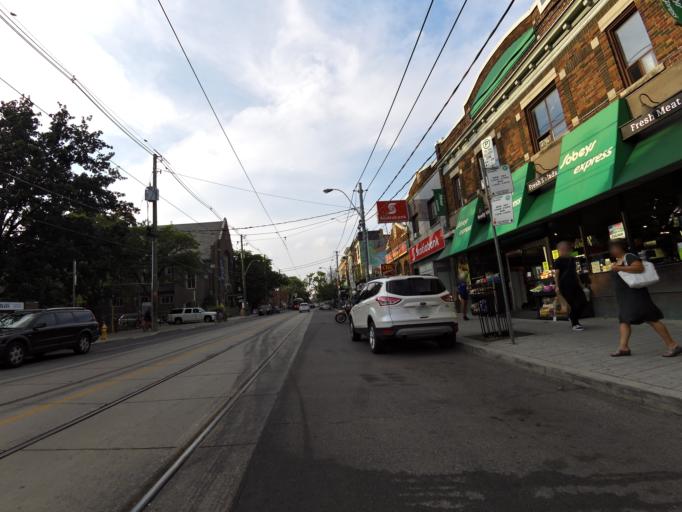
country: CA
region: Ontario
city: Toronto
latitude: 43.6447
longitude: -79.4487
